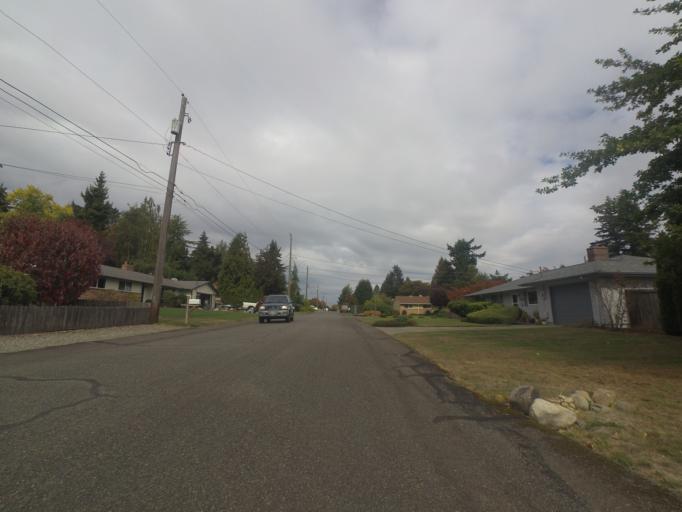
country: US
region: Washington
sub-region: Pierce County
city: University Place
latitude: 47.2146
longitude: -122.5419
